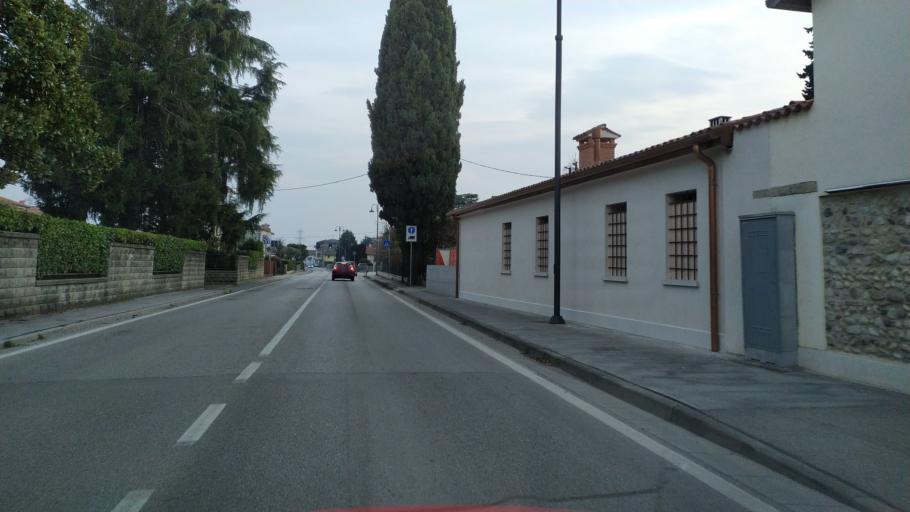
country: IT
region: Veneto
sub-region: Provincia di Vicenza
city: Montecchio Precalcino
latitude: 45.6673
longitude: 11.5632
